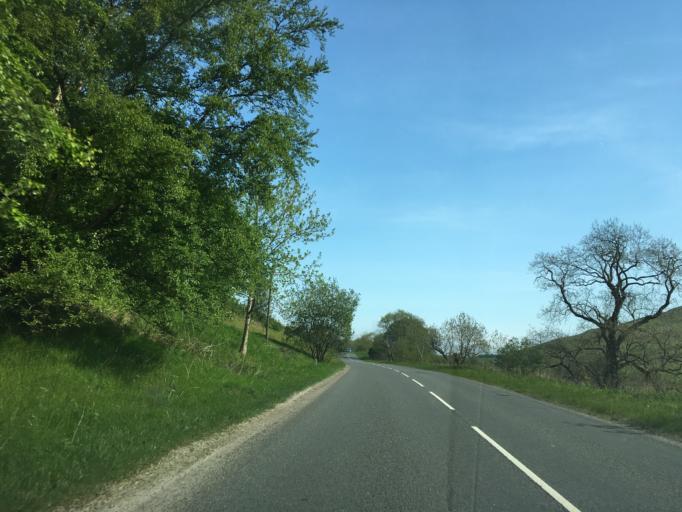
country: GB
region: Scotland
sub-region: South Lanarkshire
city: Biggar
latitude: 55.6586
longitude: -3.4311
